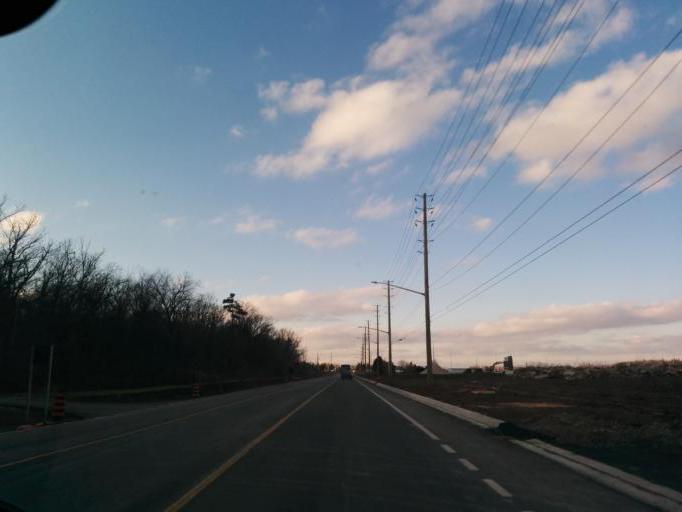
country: CA
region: Ontario
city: Oakville
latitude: 43.4893
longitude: -79.6783
